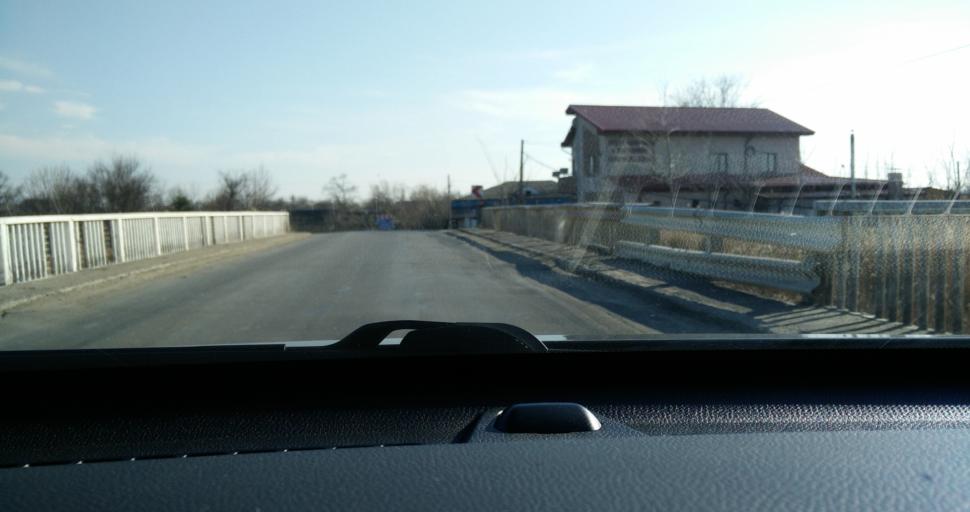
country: RO
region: Vrancea
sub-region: Comuna Maicanesti
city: Maicanesti
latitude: 45.5032
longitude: 27.4860
